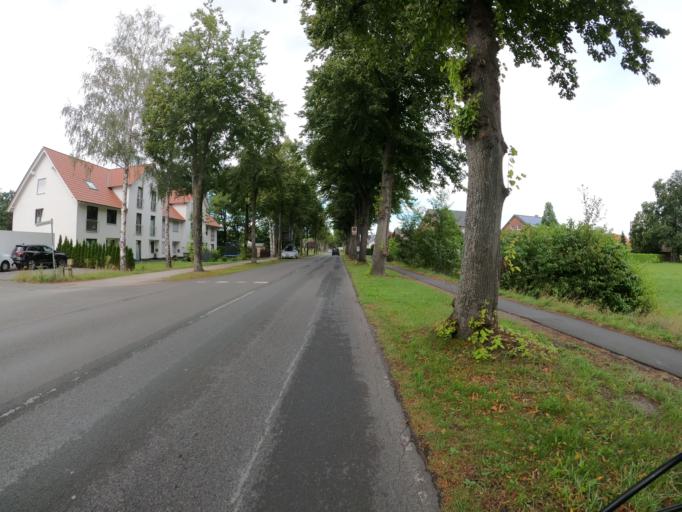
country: DE
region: North Rhine-Westphalia
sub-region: Regierungsbezirk Arnsberg
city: Lippstadt
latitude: 51.7058
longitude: 8.3385
